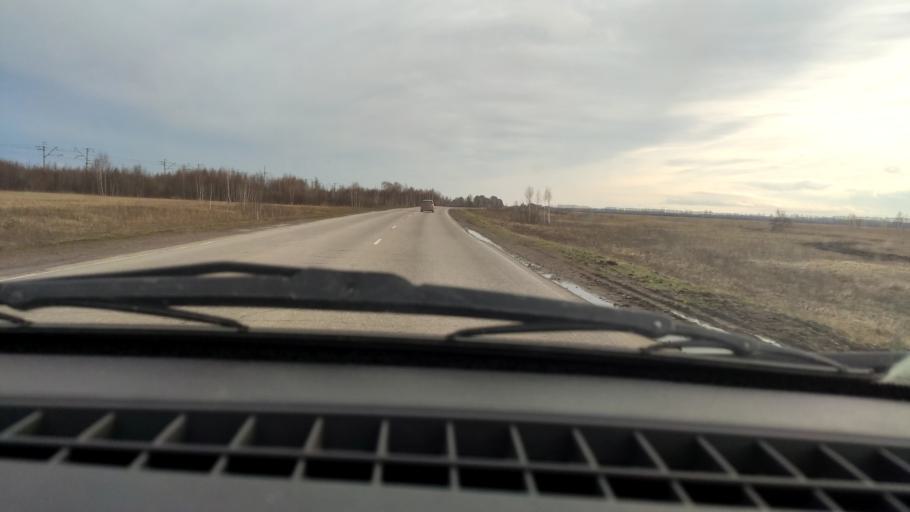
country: RU
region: Bashkortostan
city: Chishmy
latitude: 54.4304
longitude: 55.2343
